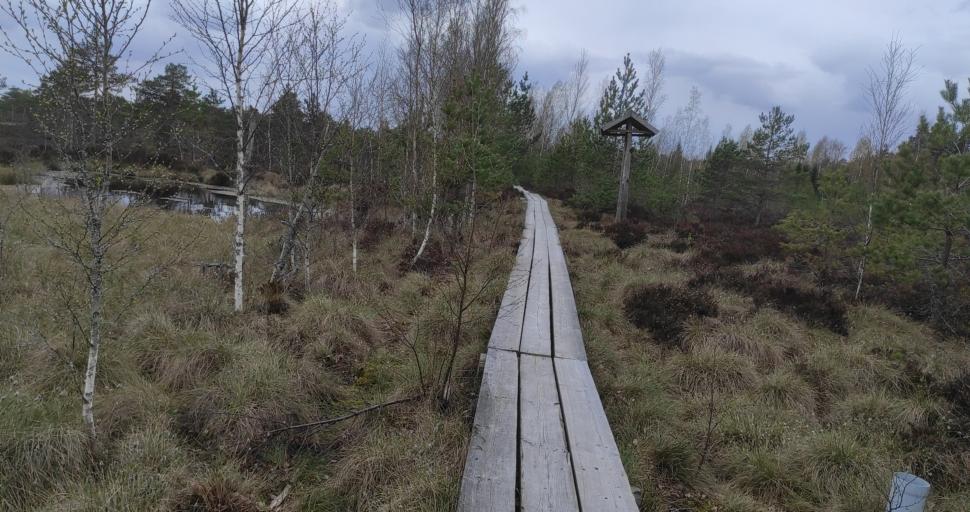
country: LV
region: Dundaga
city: Dundaga
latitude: 57.3549
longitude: 22.1532
